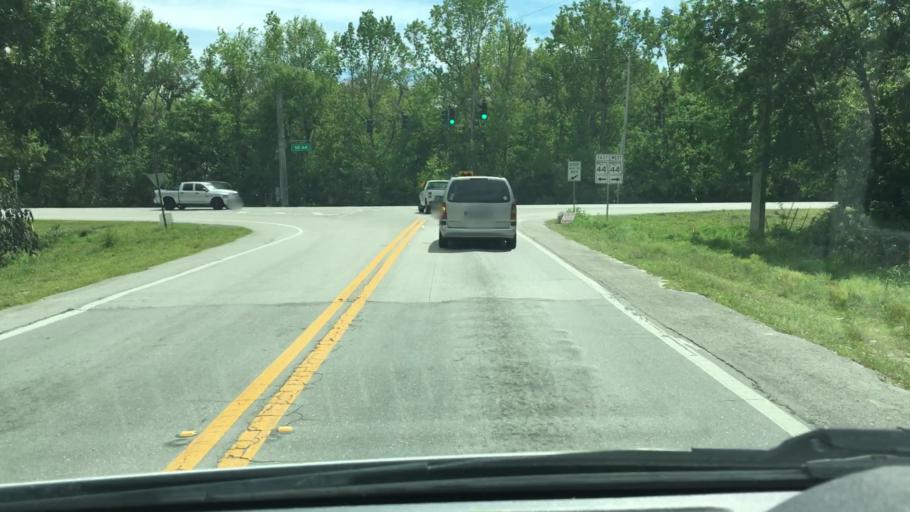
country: US
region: Florida
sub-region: Lake County
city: Lake Mack-Forest Hills
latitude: 29.0058
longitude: -81.3862
